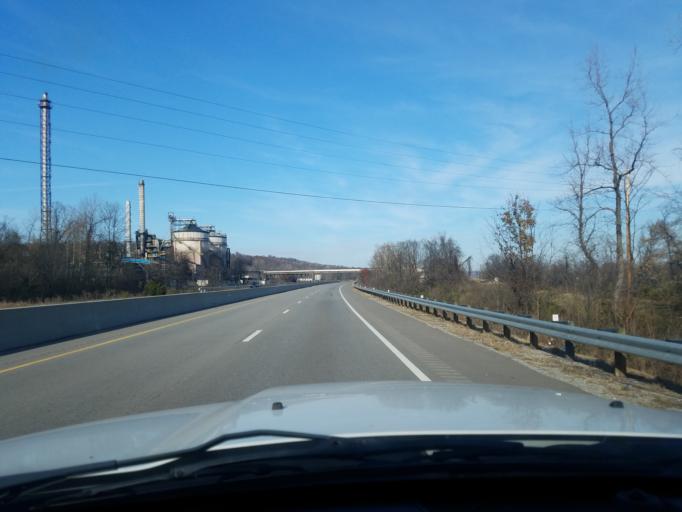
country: US
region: Ohio
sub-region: Washington County
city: Belpre
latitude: 39.2989
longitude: -81.5671
